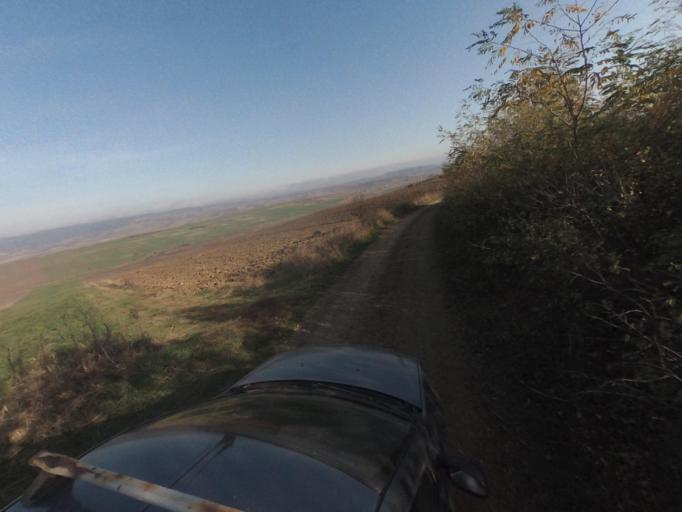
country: RO
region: Neamt
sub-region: Comuna Pancesti
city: Pancesti
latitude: 46.8783
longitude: 27.1911
